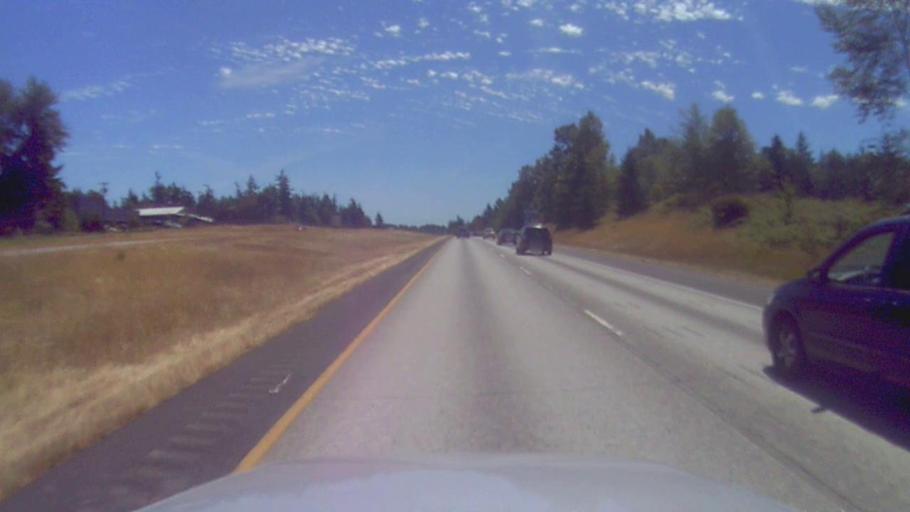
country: US
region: Washington
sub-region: Whatcom County
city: Marietta-Alderwood
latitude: 48.7967
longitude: -122.5285
